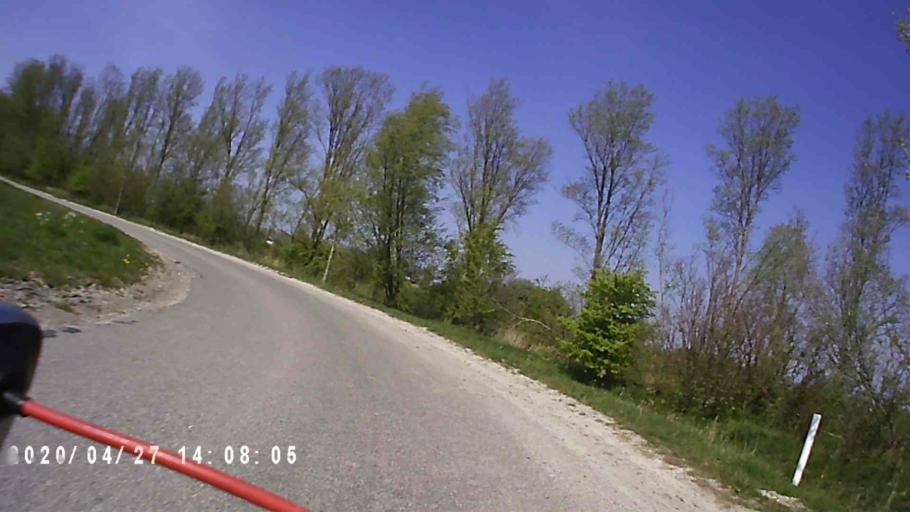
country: NL
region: Groningen
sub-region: Gemeente Zuidhorn
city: Oldehove
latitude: 53.3454
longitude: 6.3949
